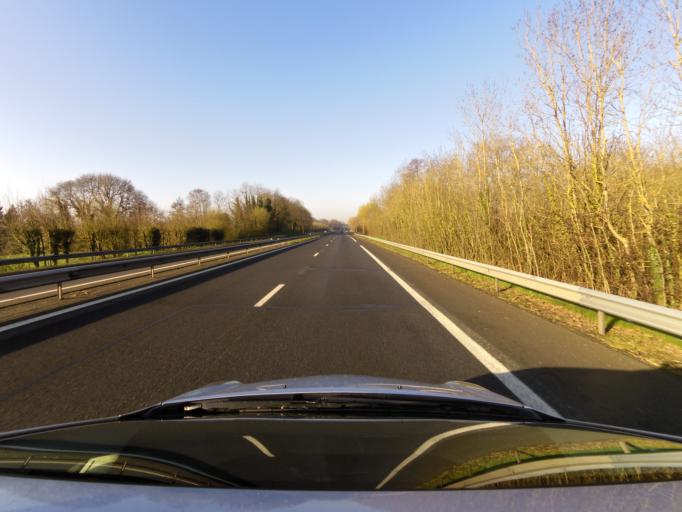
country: FR
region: Lower Normandy
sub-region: Departement du Calvados
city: Tourville-sur-Odon
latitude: 49.1509
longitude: -0.5042
